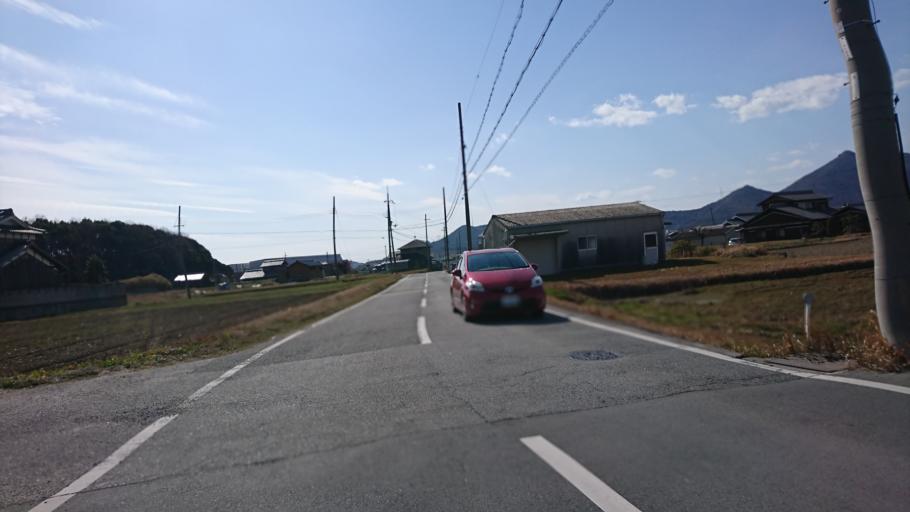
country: JP
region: Hyogo
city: Kakogawacho-honmachi
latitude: 34.8120
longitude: 134.8266
